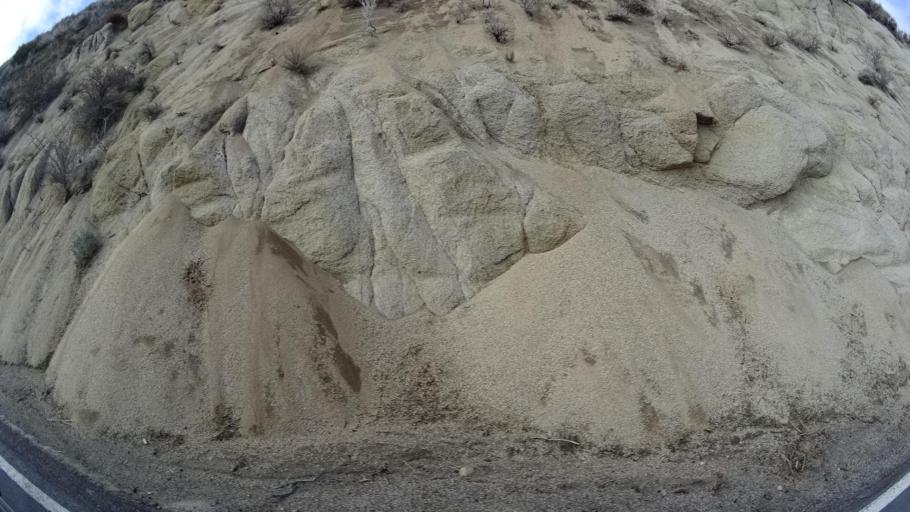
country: US
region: Nevada
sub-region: Washoe County
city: Cold Springs
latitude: 39.8209
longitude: -119.9368
